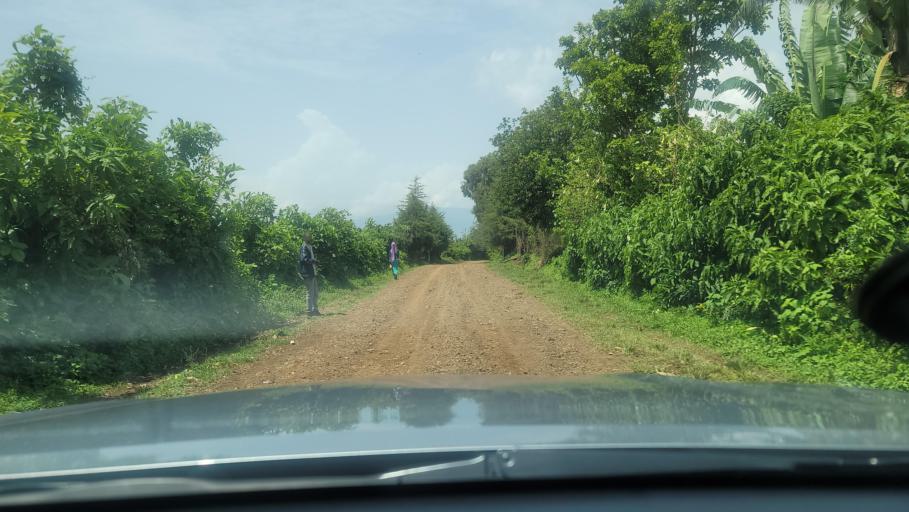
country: ET
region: Oromiya
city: Agaro
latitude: 7.8303
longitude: 36.4070
